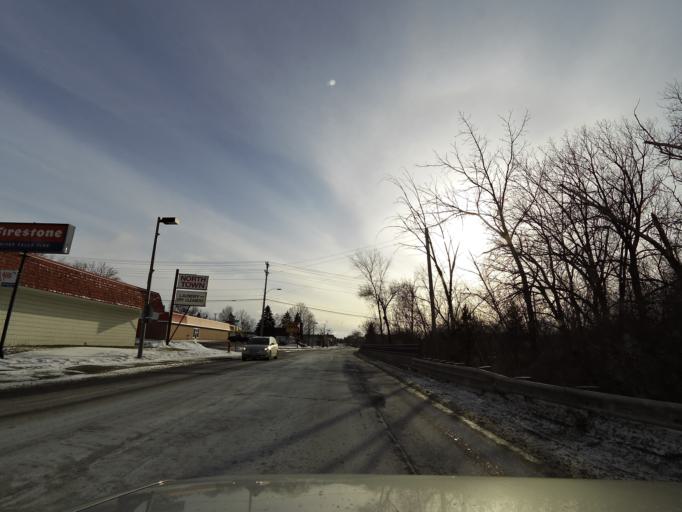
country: US
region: Wisconsin
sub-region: Pierce County
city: River Falls
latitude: 44.8622
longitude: -92.6241
